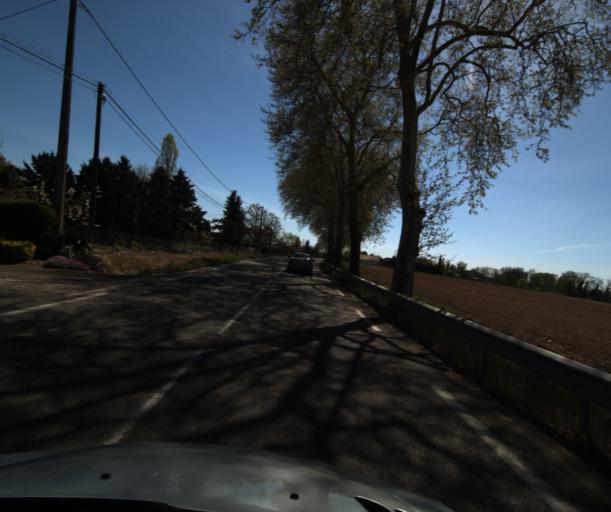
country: FR
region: Midi-Pyrenees
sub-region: Departement du Tarn-et-Garonne
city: Montbeton
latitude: 44.0668
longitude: 1.2866
